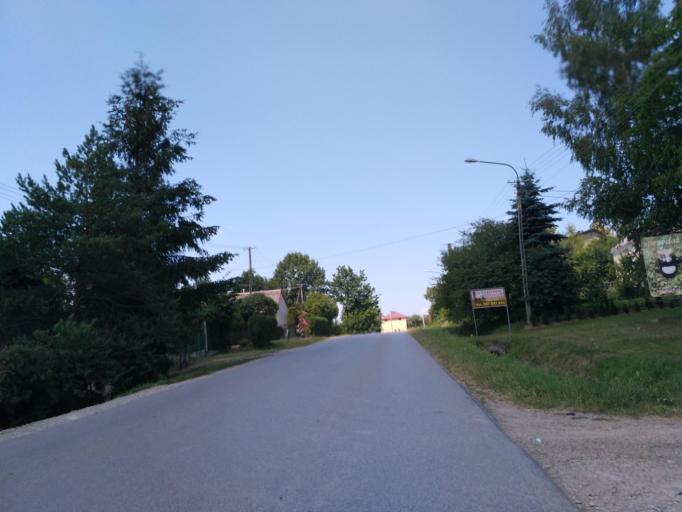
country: PL
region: Subcarpathian Voivodeship
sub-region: Powiat sanocki
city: Niebieszczany
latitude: 49.5155
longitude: 22.1395
